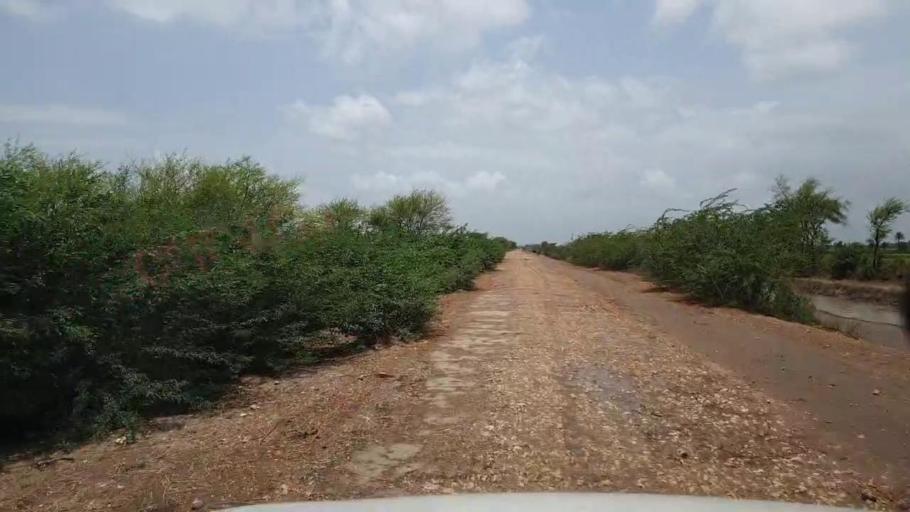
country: PK
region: Sindh
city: Kario
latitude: 24.7111
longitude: 68.5971
